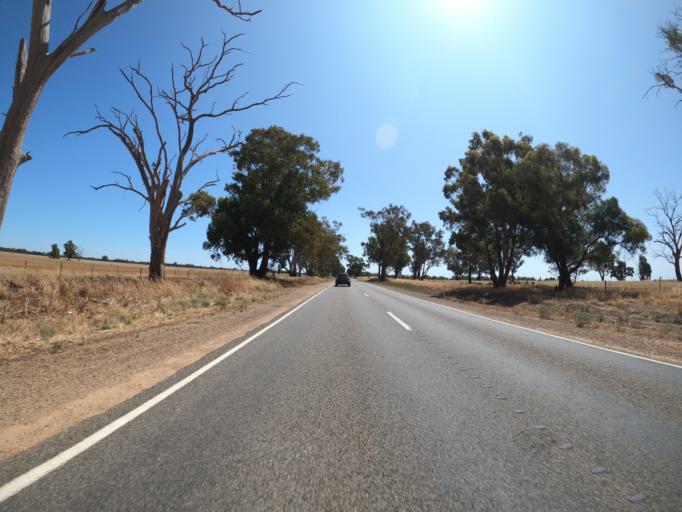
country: AU
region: Victoria
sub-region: Moira
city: Yarrawonga
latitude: -36.0247
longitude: 146.1054
